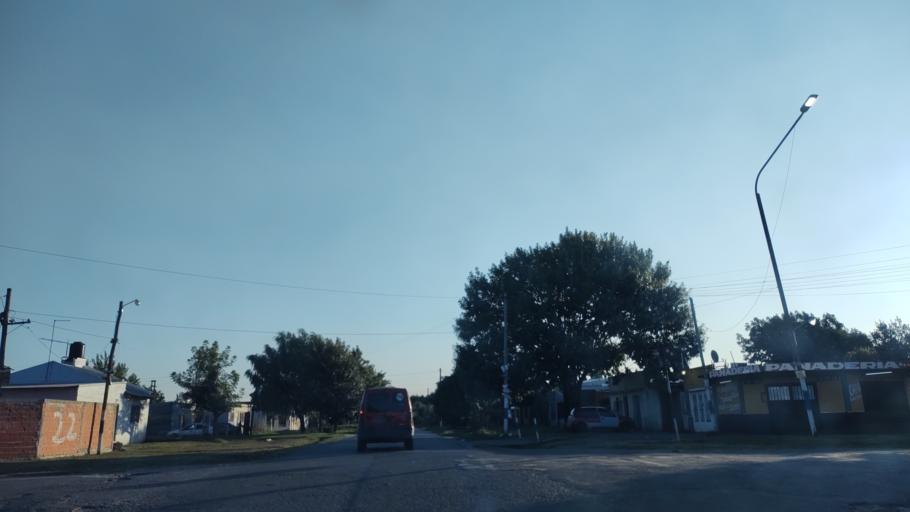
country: AR
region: Buenos Aires
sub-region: Partido de La Plata
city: La Plata
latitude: -34.9707
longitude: -57.9714
